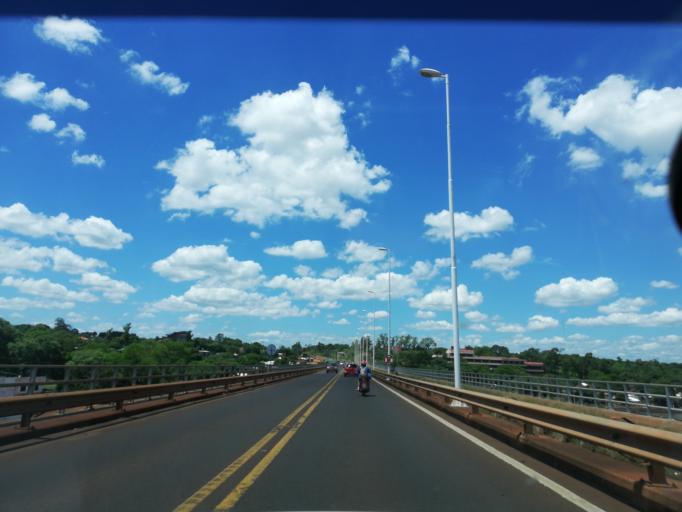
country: AR
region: Misiones
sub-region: Departamento de Capital
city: Posadas
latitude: -27.3681
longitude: -55.8589
